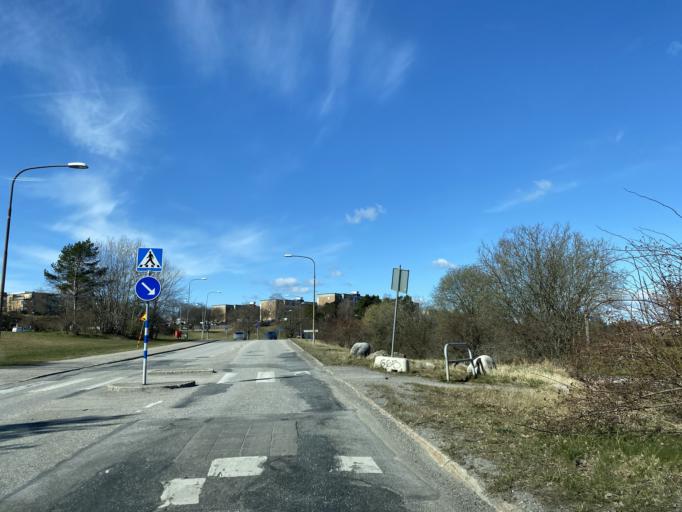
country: SE
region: Stockholm
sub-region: Stockholms Kommun
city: Arsta
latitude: 59.2886
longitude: 18.0406
